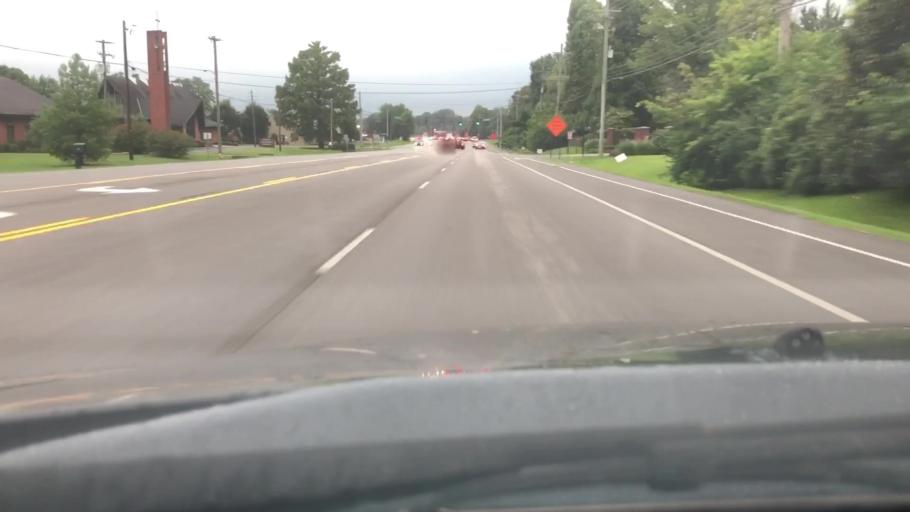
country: US
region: Kentucky
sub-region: Jefferson County
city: Hurstbourne Acres
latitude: 38.2100
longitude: -85.5854
